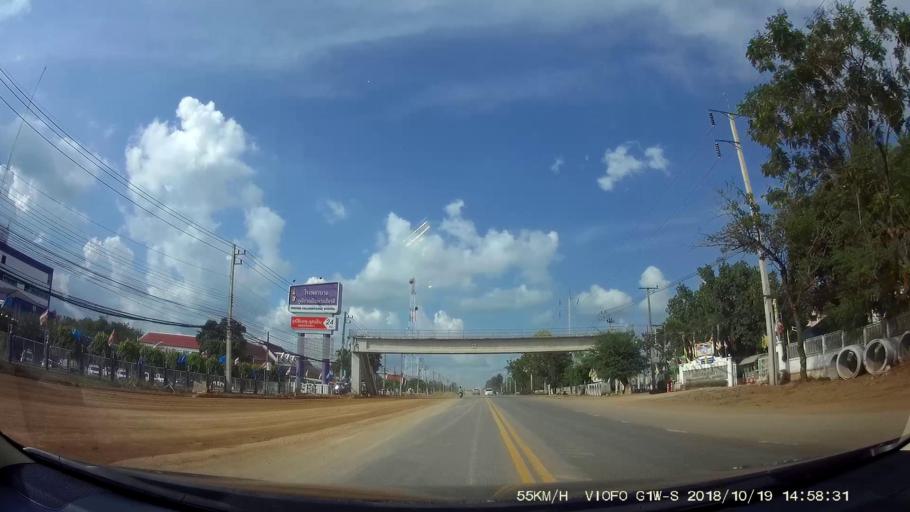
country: TH
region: Chaiyaphum
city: Phu Khiao
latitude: 16.3755
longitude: 102.1293
